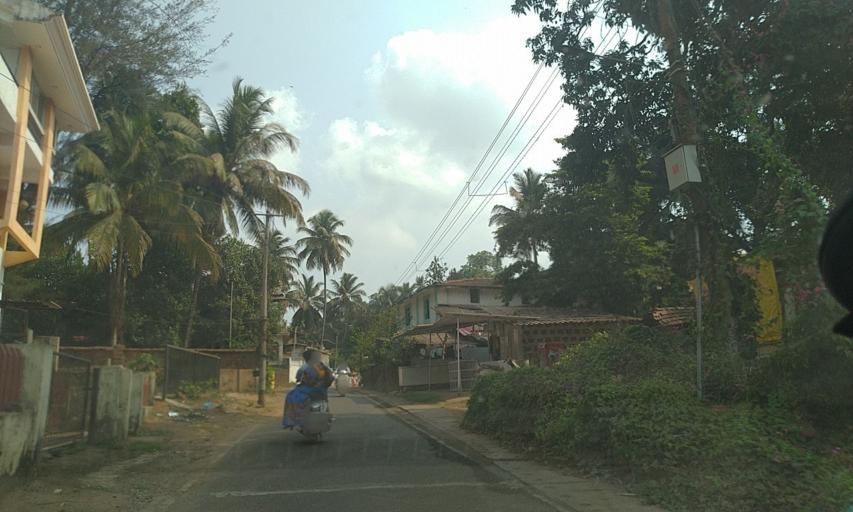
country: IN
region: Goa
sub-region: North Goa
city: Taleigao
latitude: 15.4749
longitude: 73.8435
